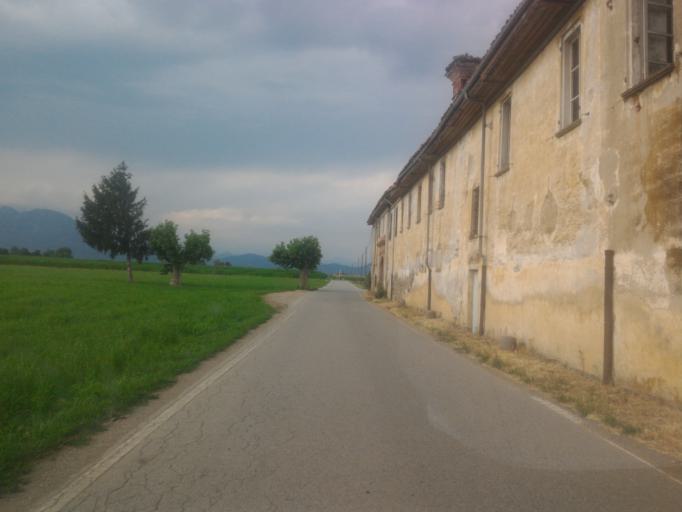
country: IT
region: Piedmont
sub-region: Provincia di Torino
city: Buriasco
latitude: 44.8800
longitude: 7.4021
